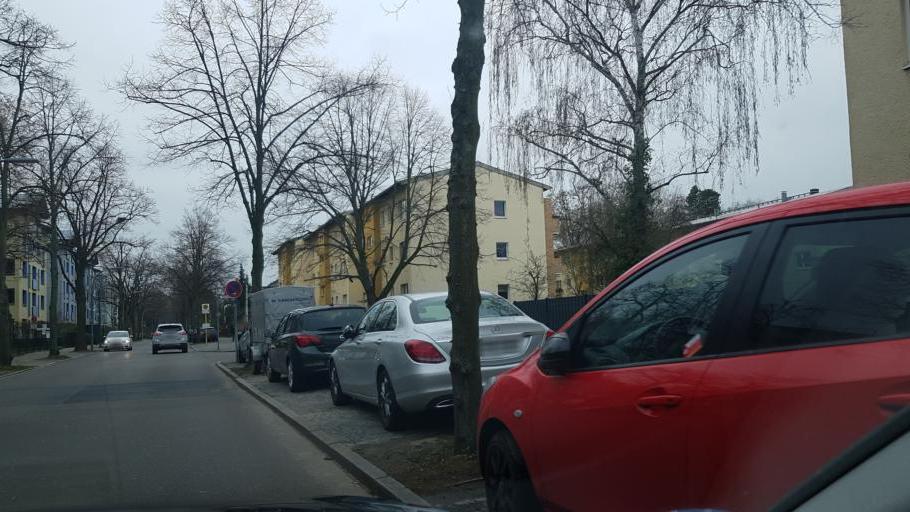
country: DE
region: Berlin
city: Lichtenrade
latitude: 52.3942
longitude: 13.3979
